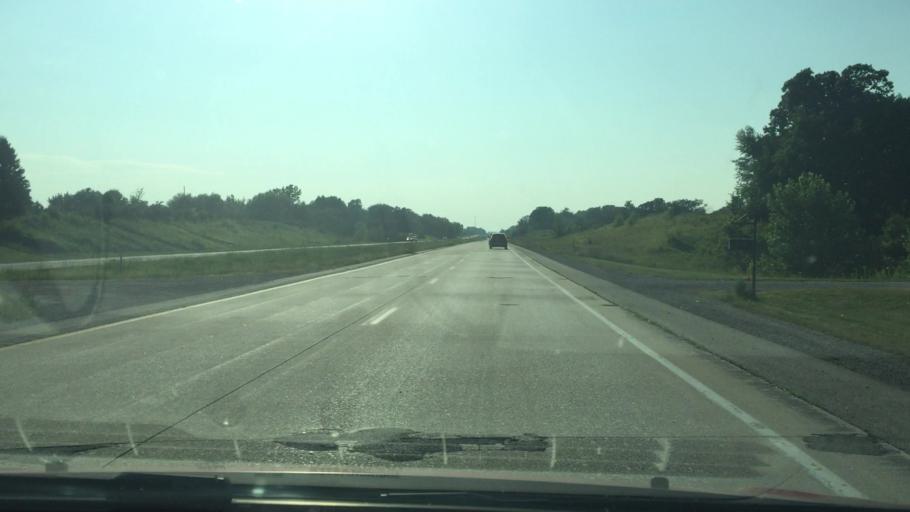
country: US
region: Iowa
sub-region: Scott County
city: Blue Grass
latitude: 41.5144
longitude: -90.8150
